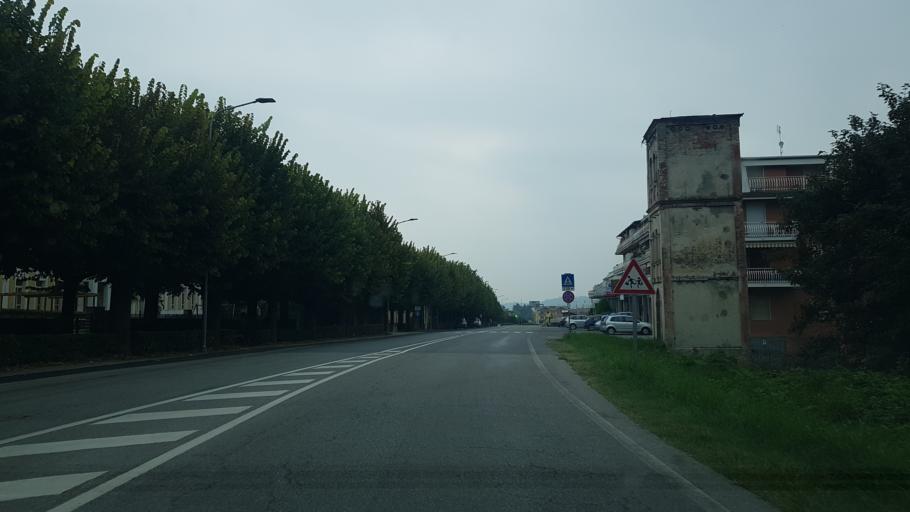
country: IT
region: Piedmont
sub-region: Provincia di Cuneo
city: Villanova Mondovi
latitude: 44.3461
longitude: 7.7671
